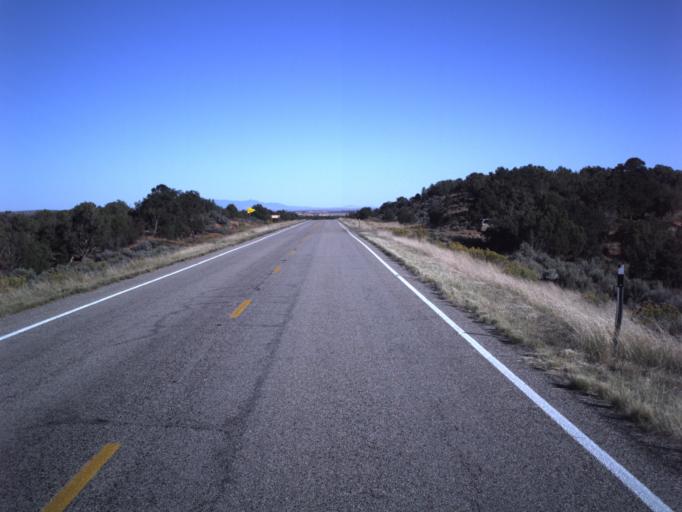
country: US
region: Utah
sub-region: San Juan County
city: Blanding
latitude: 37.5354
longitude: -109.7341
